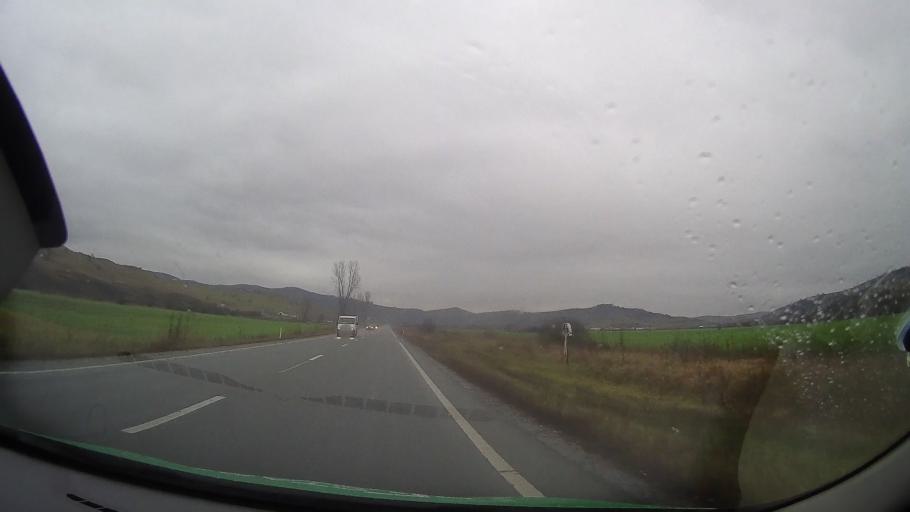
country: RO
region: Bistrita-Nasaud
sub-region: Comuna Teaca
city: Teaca
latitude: 46.9246
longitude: 24.4875
